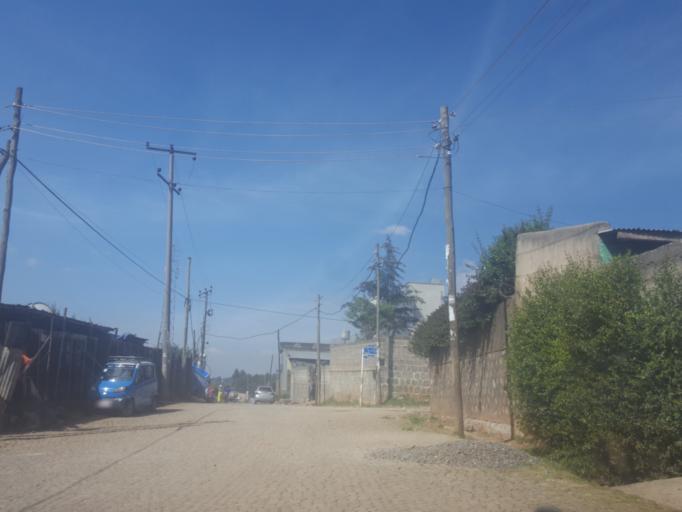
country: ET
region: Adis Abeba
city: Addis Ababa
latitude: 9.0686
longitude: 38.7312
